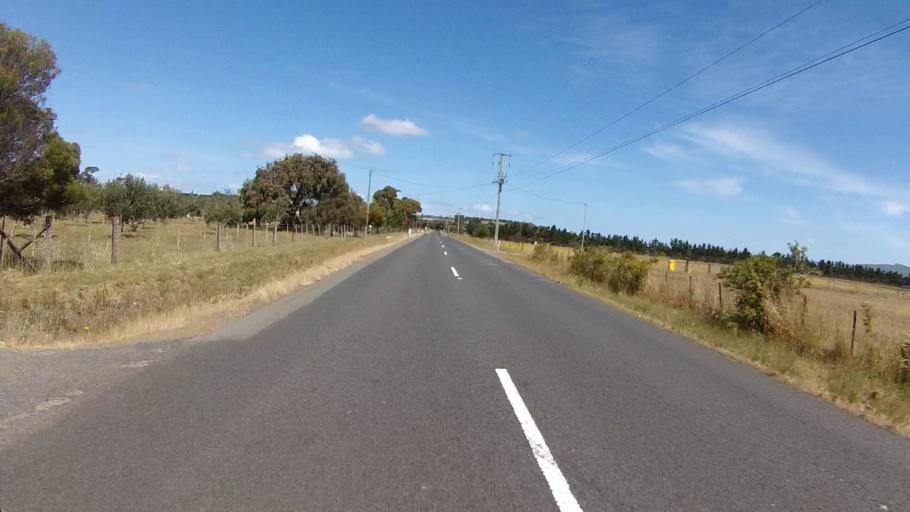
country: AU
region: Tasmania
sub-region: Sorell
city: Sorell
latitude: -42.7750
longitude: 147.5196
